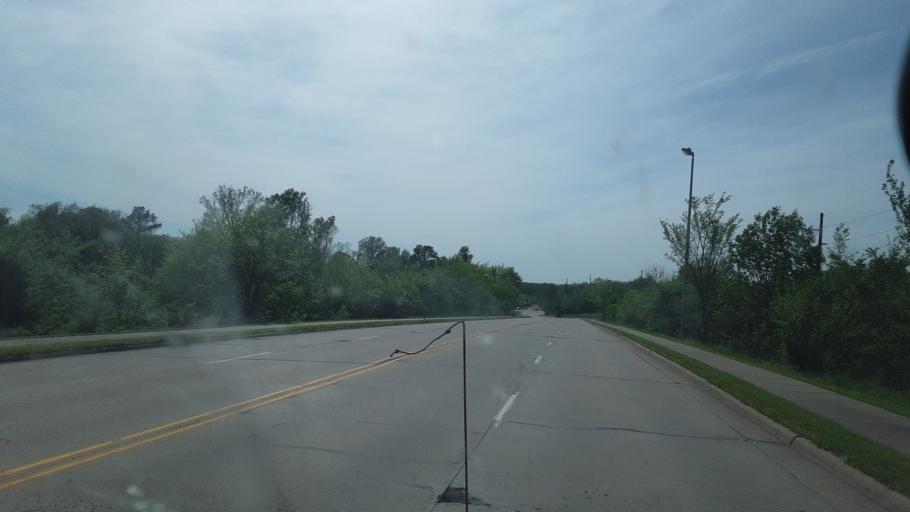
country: US
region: Illinois
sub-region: Jackson County
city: Carbondale
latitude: 37.7004
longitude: -89.2131
